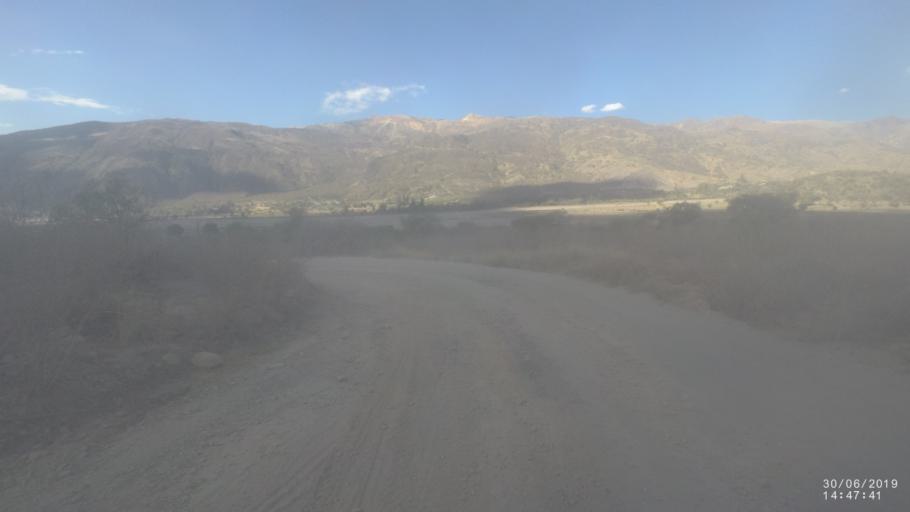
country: BO
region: Cochabamba
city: Irpa Irpa
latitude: -17.7929
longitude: -66.3456
